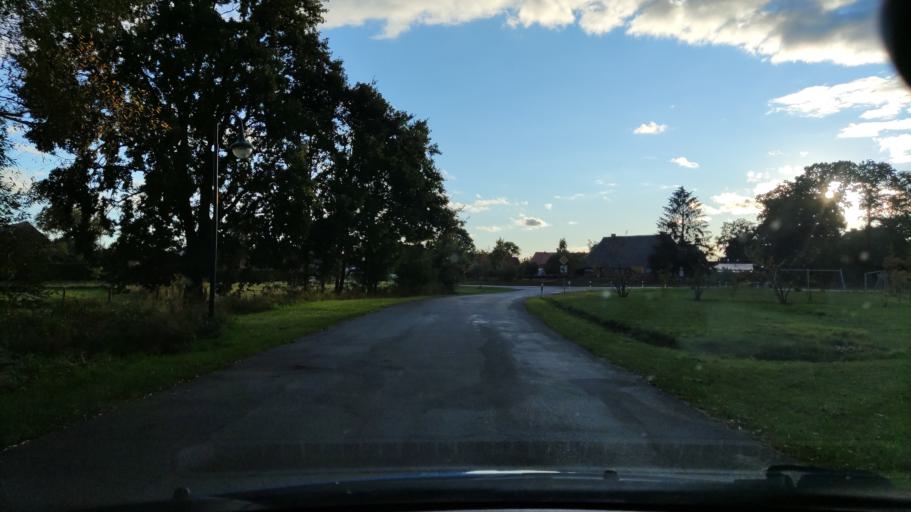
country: DE
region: Lower Saxony
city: Neu Darchau
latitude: 53.3421
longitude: 10.8606
